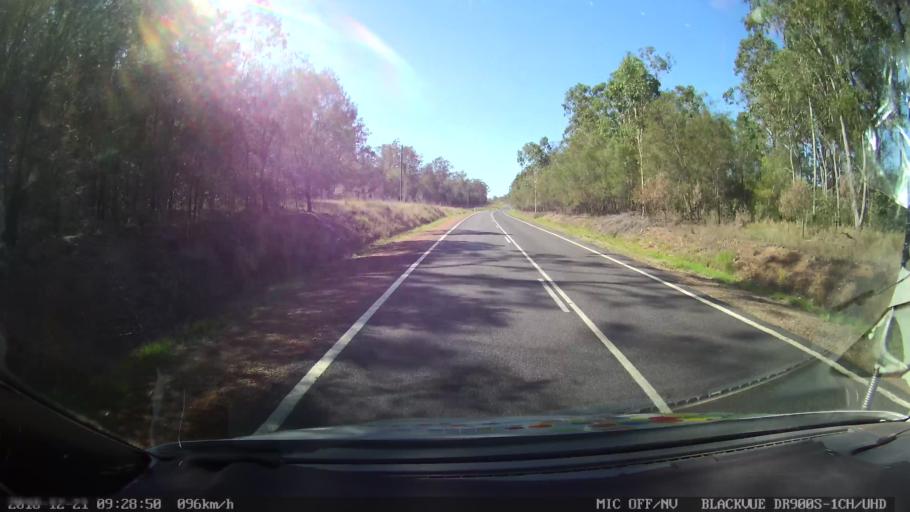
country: AU
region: New South Wales
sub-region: Clarence Valley
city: Maclean
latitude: -29.4231
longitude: 152.9884
